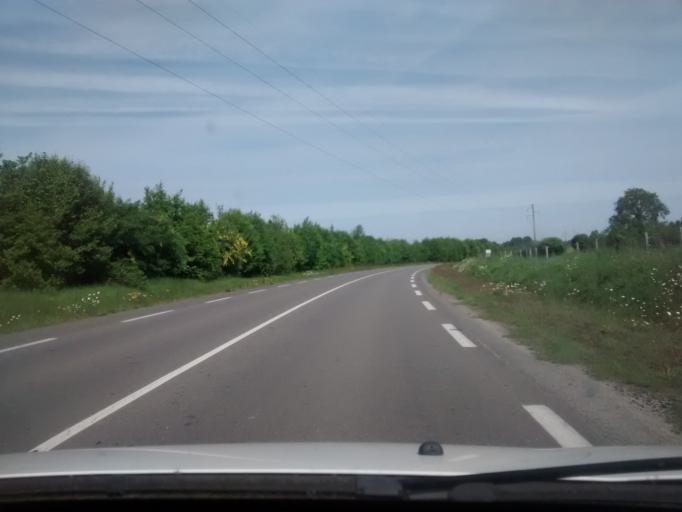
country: FR
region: Brittany
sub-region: Departement d'Ille-et-Vilaine
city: Saint-Brice-en-Cogles
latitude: 48.4011
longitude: -1.3765
